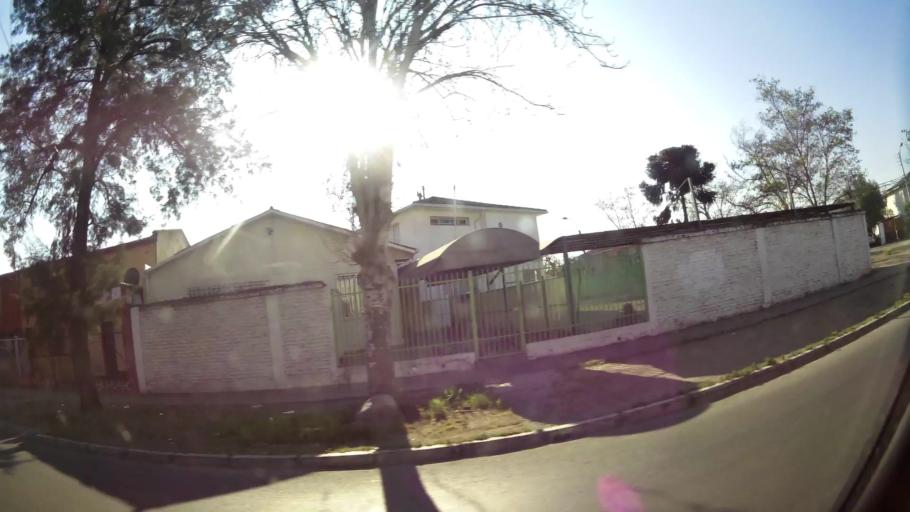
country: CL
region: Santiago Metropolitan
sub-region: Provincia de Santiago
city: Santiago
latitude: -33.4794
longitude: -70.6305
